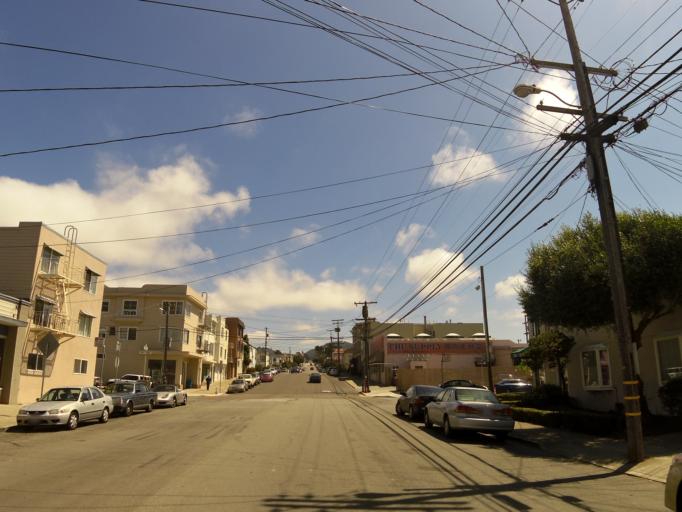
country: US
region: California
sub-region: San Mateo County
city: Daly City
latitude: 37.7386
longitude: -122.4920
